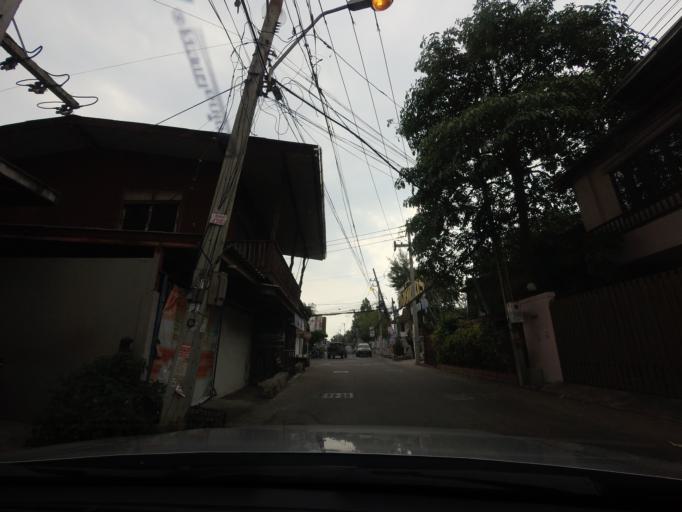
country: TH
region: Chon Buri
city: Phatthaya
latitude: 12.9780
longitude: 100.9109
